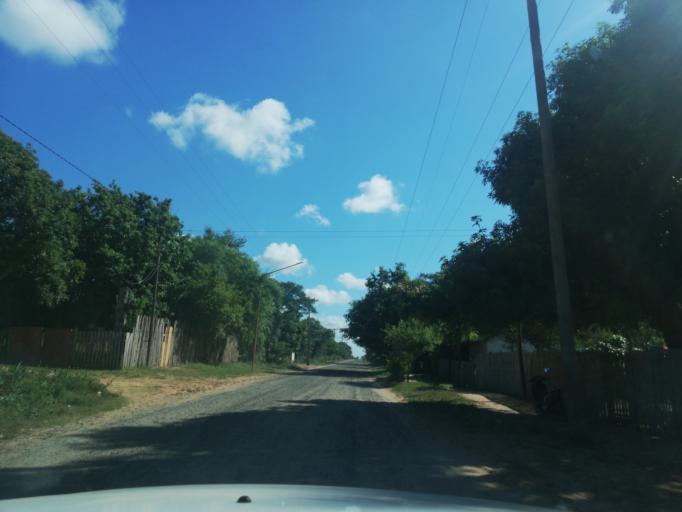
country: AR
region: Corrientes
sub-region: Departamento de San Miguel
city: San Miguel
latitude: -27.9897
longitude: -57.5874
